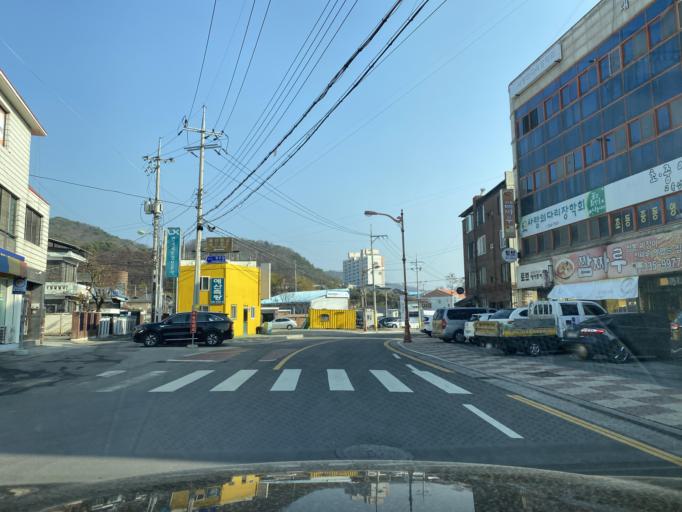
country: KR
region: Chungcheongnam-do
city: Yesan
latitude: 36.6822
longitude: 126.8502
